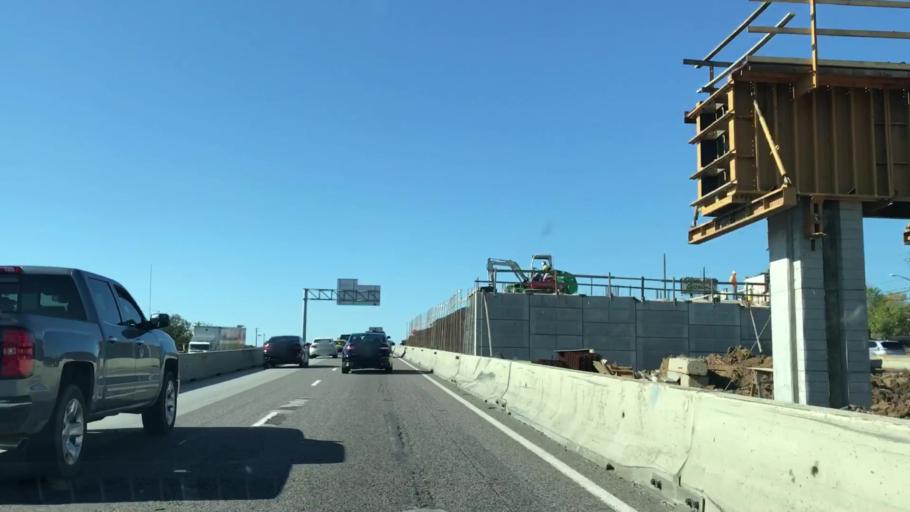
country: US
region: Texas
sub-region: Denton County
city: Corinth
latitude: 33.1812
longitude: -97.1010
